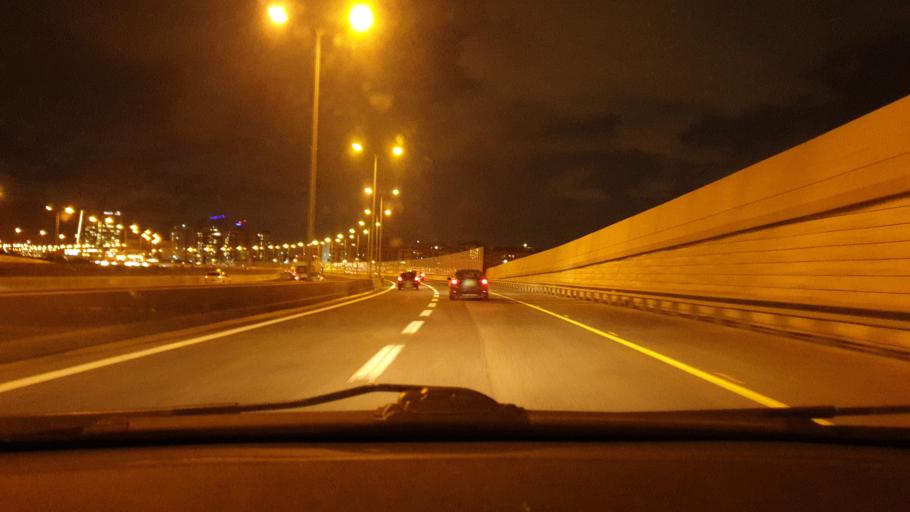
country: IL
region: Central District
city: Ness Ziona
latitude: 31.9440
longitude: 34.8146
